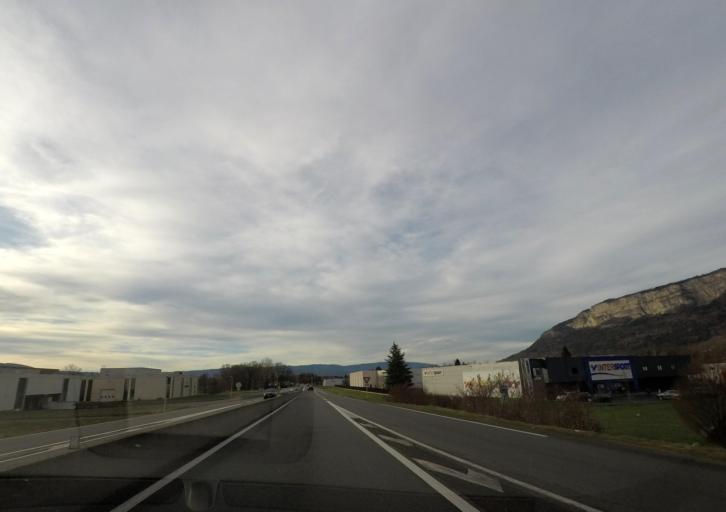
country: FR
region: Rhone-Alpes
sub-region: Departement de la Haute-Savoie
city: Bonneville
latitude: 46.0723
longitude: 6.4186
